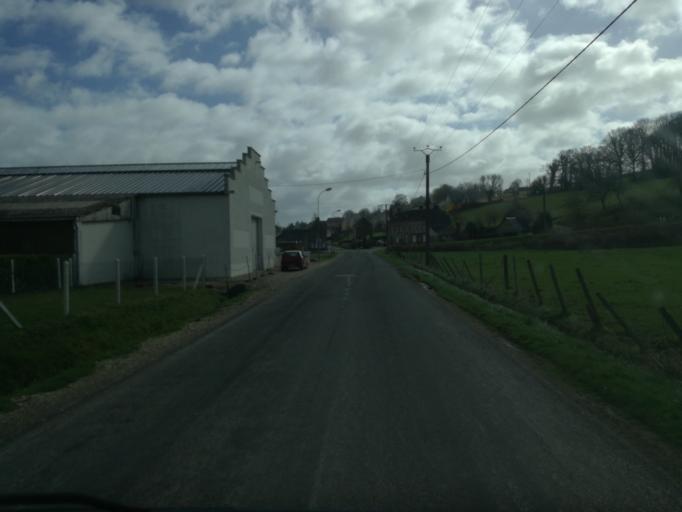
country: FR
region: Haute-Normandie
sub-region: Departement de la Seine-Maritime
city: Bretteville-du-Grand-Caux
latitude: 49.7048
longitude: 0.4423
